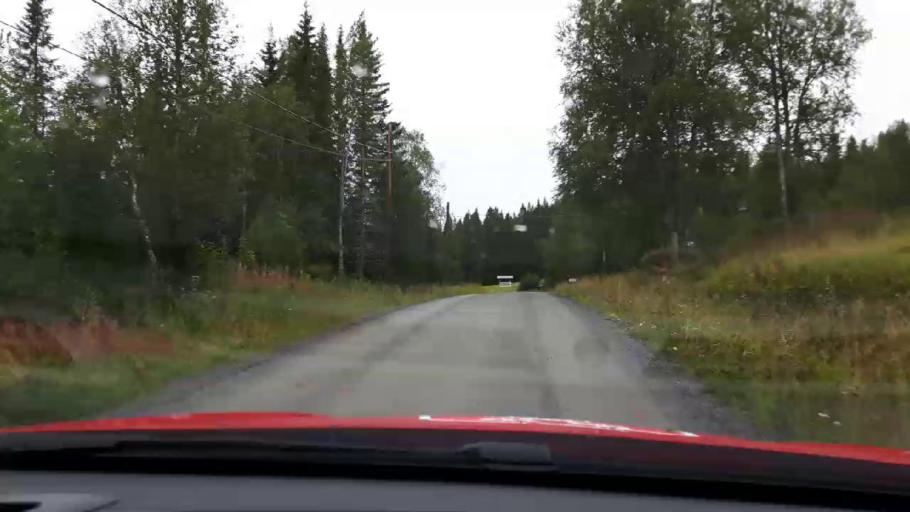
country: SE
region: Jaemtland
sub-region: Are Kommun
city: Are
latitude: 63.5020
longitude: 12.7524
